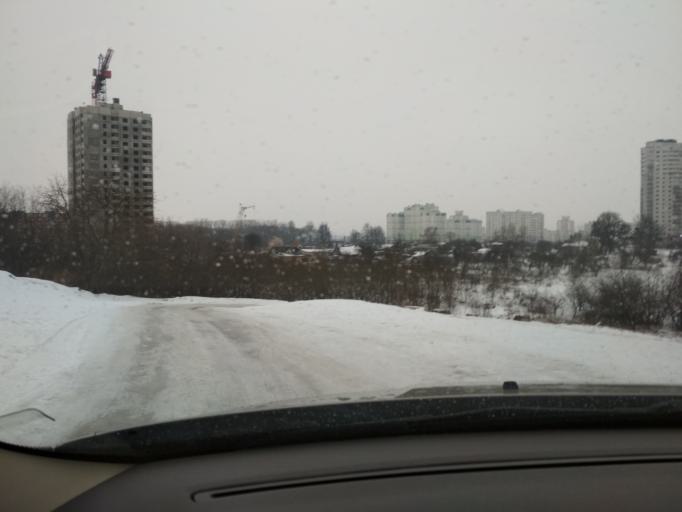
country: BY
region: Minsk
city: Novoye Medvezhino
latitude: 53.9046
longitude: 27.4288
